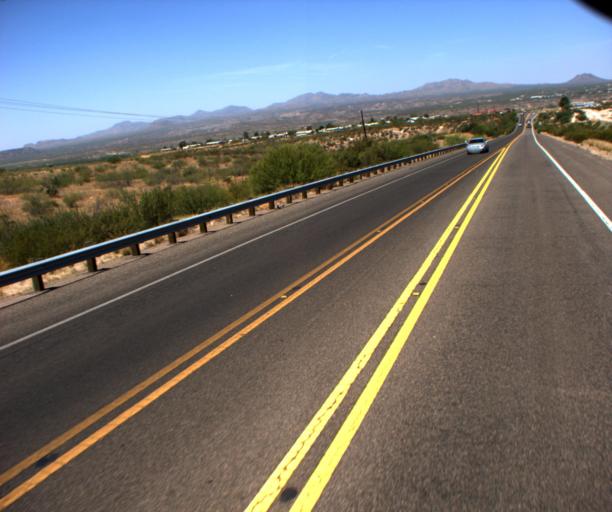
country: US
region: Arizona
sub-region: Gila County
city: Peridot
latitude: 33.2921
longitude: -110.4295
